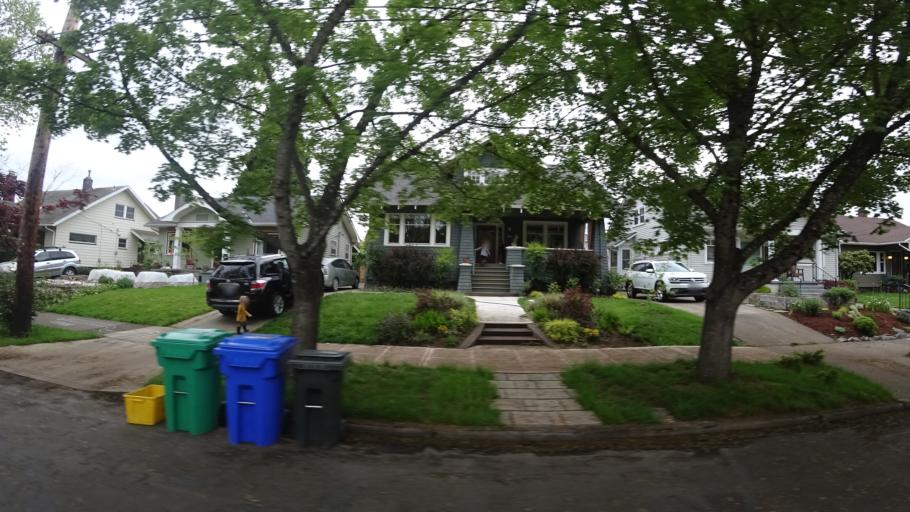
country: US
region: Oregon
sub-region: Clackamas County
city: Milwaukie
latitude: 45.4782
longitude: -122.6463
